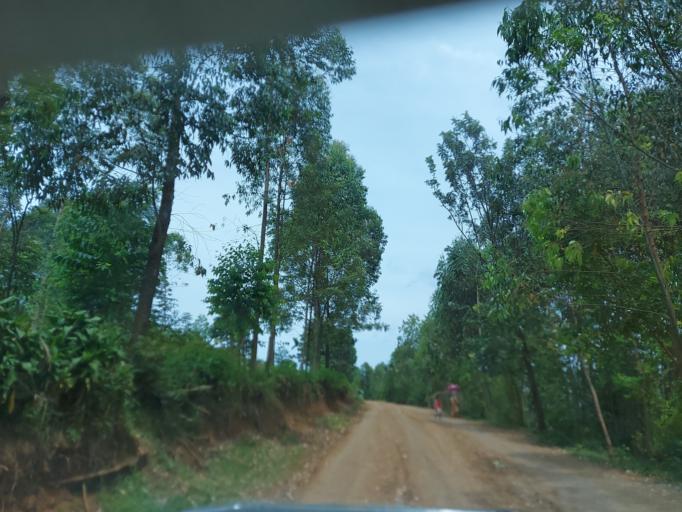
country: CD
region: South Kivu
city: Bukavu
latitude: -2.2374
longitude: 28.8421
